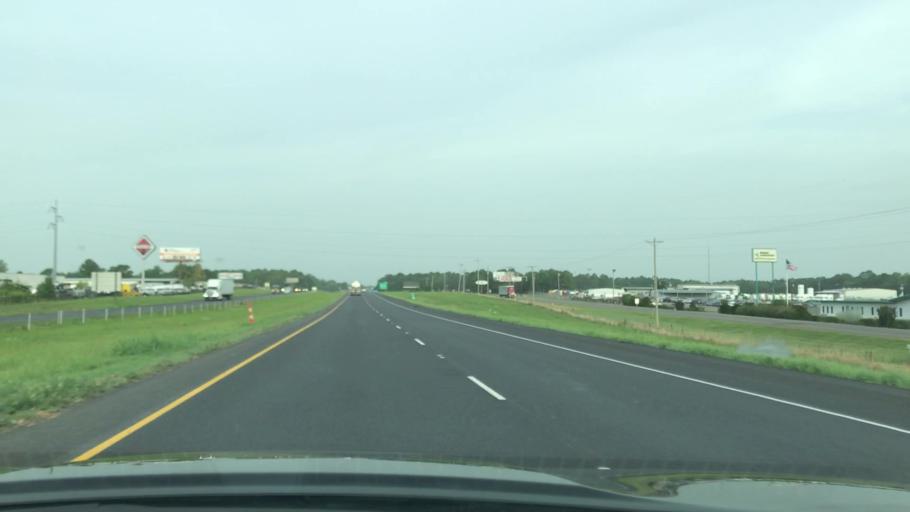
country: US
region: Louisiana
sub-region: Caddo Parish
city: Greenwood
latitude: 32.4453
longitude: -93.9219
